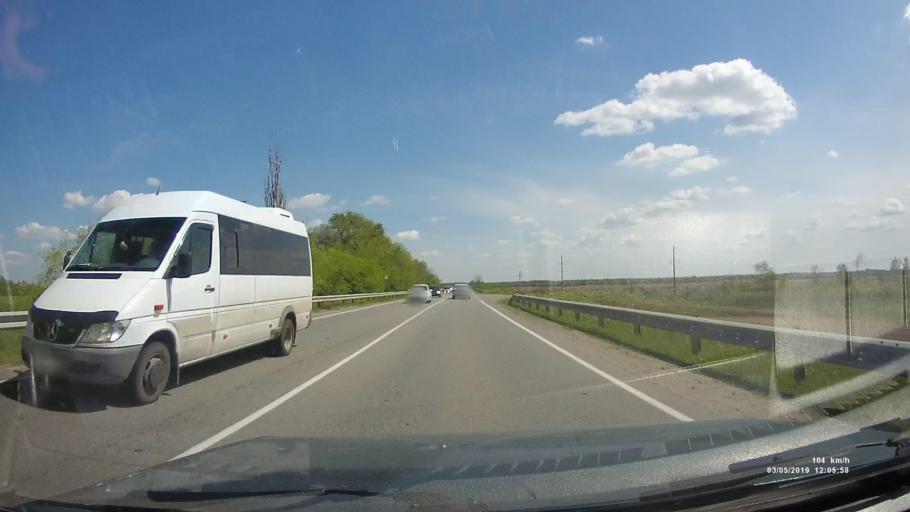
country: RU
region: Rostov
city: Bagayevskaya
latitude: 47.2864
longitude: 40.4410
